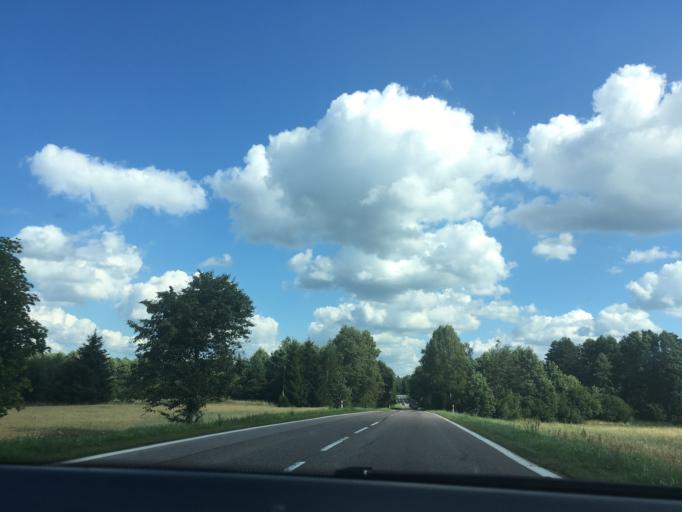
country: PL
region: Podlasie
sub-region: Powiat bialostocki
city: Wasilkow
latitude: 53.3294
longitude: 23.1162
